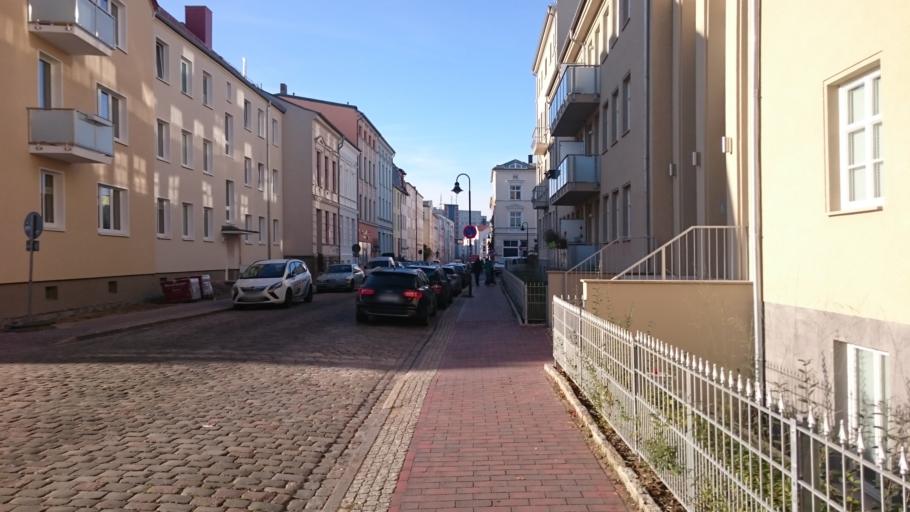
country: DE
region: Mecklenburg-Vorpommern
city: Rostock
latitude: 54.0841
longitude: 12.1316
